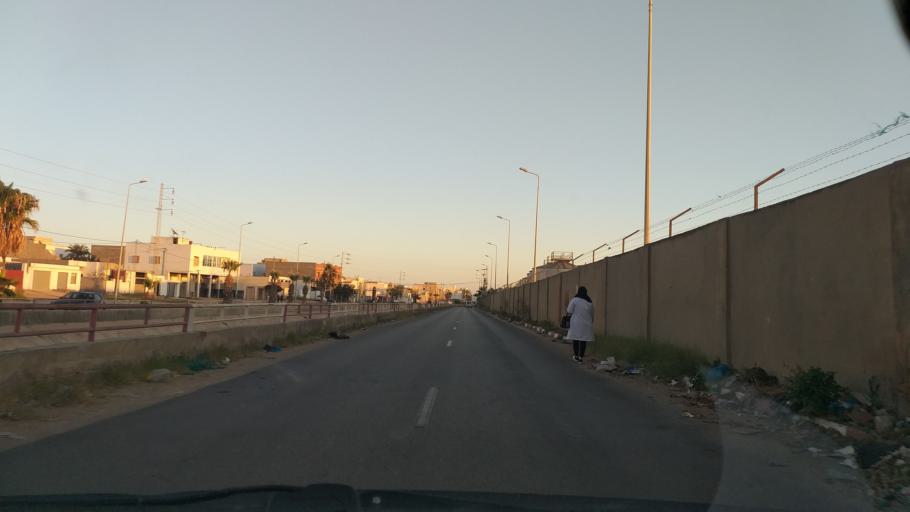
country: TN
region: Safaqis
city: Al Qarmadah
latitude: 34.7677
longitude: 10.7752
